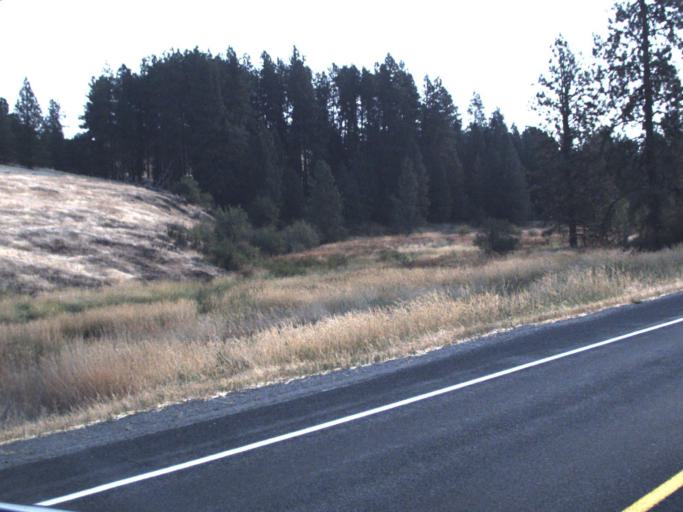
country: US
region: Washington
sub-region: Spokane County
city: Veradale
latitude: 47.4439
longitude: -117.1141
